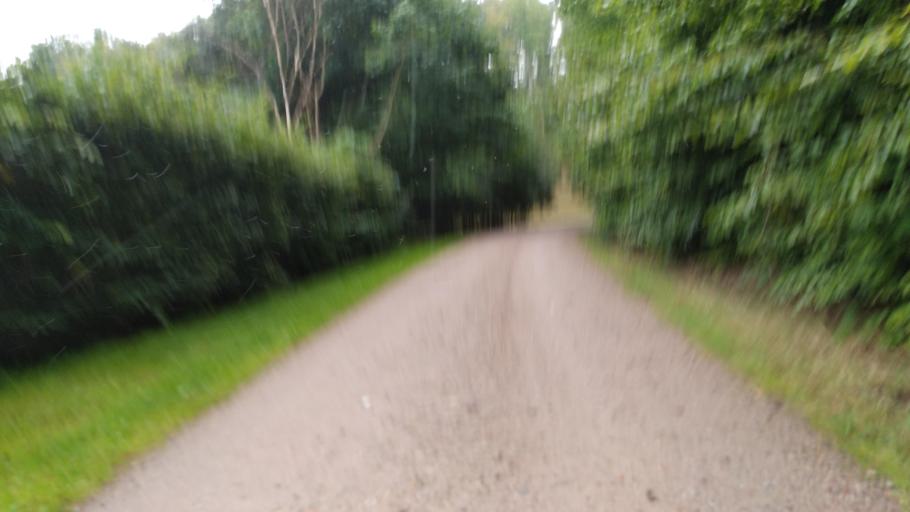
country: PL
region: Pomeranian Voivodeship
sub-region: Powiat wejherowski
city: Goscicino
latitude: 54.6331
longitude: 18.1337
